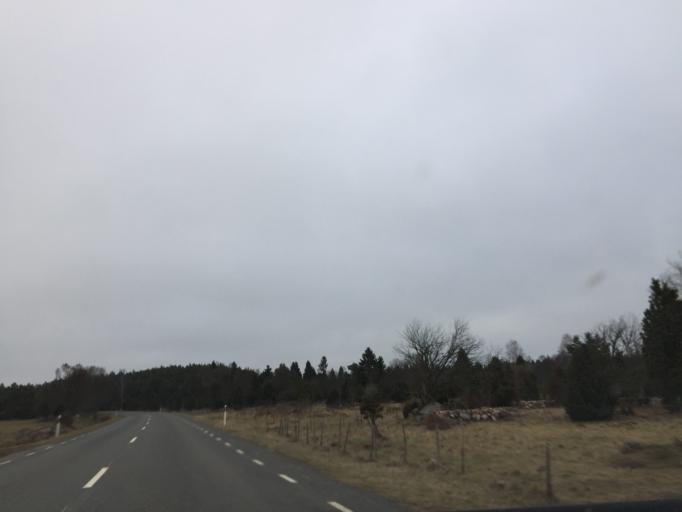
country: EE
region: Saare
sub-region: Kuressaare linn
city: Kuressaare
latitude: 58.5423
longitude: 22.3377
